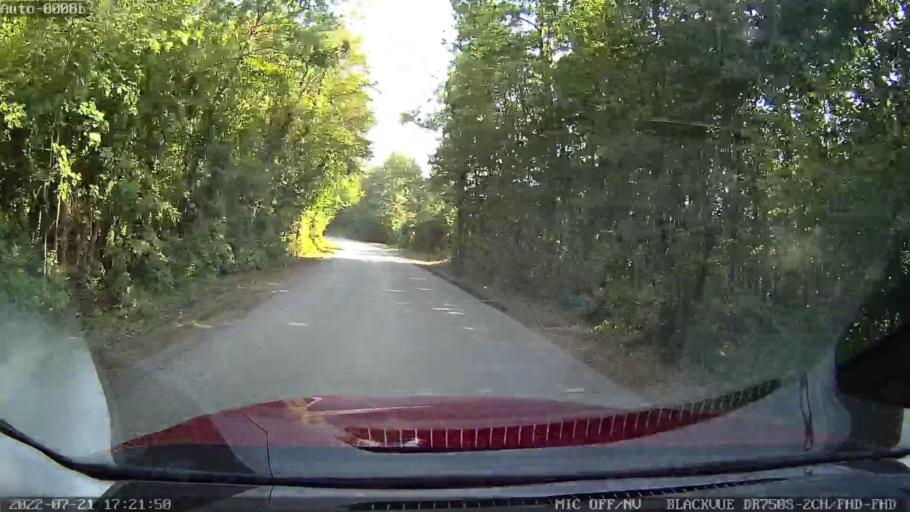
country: HR
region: Istarska
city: Karojba
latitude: 45.1918
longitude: 13.8279
